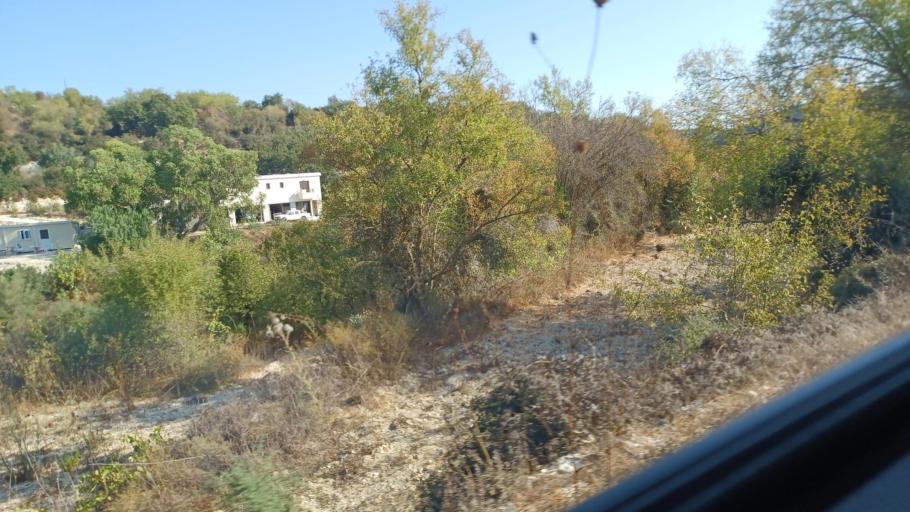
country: CY
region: Pafos
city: Mesogi
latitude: 34.8466
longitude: 32.4787
